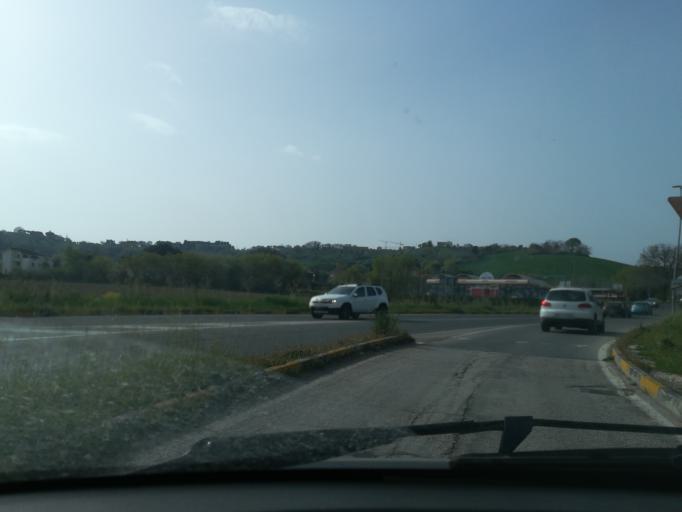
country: IT
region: The Marches
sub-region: Provincia di Macerata
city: Piediripa
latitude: 43.2814
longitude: 13.4852
